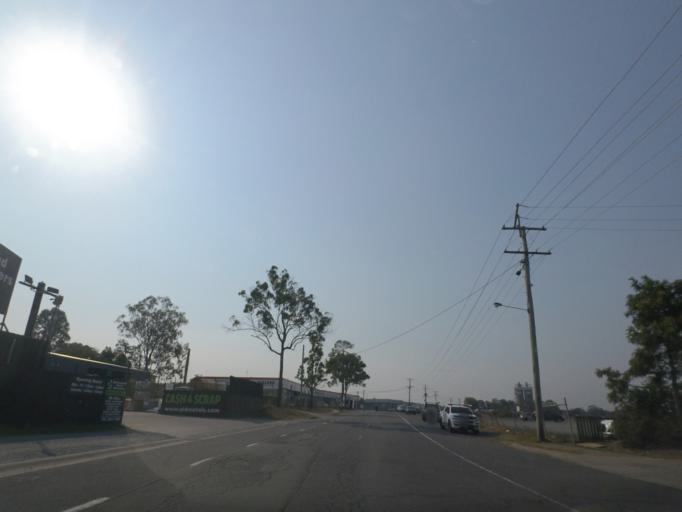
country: AU
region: Queensland
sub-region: Gold Coast
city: Yatala
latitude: -27.7352
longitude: 153.2254
